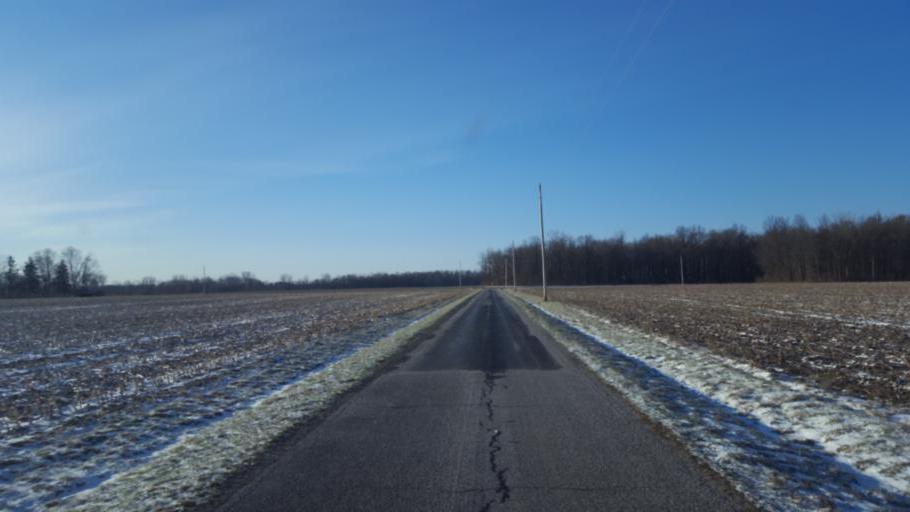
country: US
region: Ohio
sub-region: Morrow County
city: Mount Gilead
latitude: 40.6035
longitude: -82.8853
